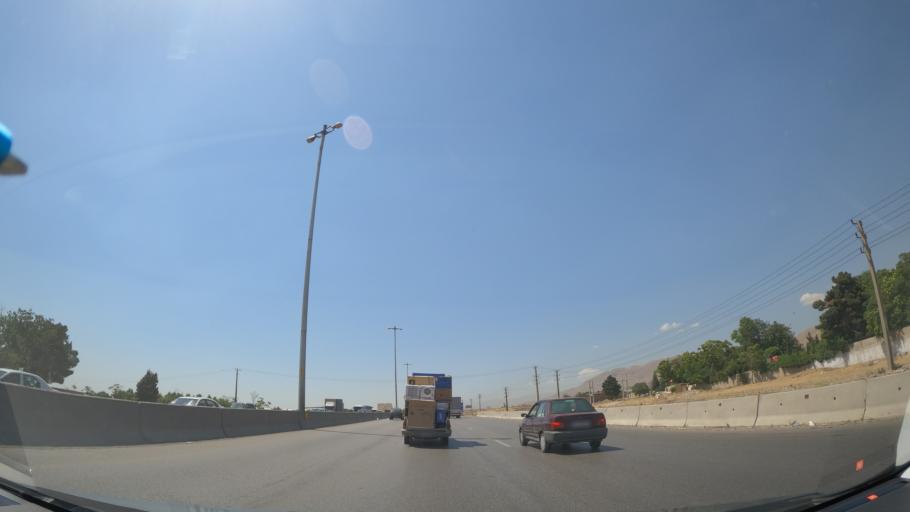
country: IR
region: Alborz
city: Karaj
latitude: 35.8726
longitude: 50.8956
